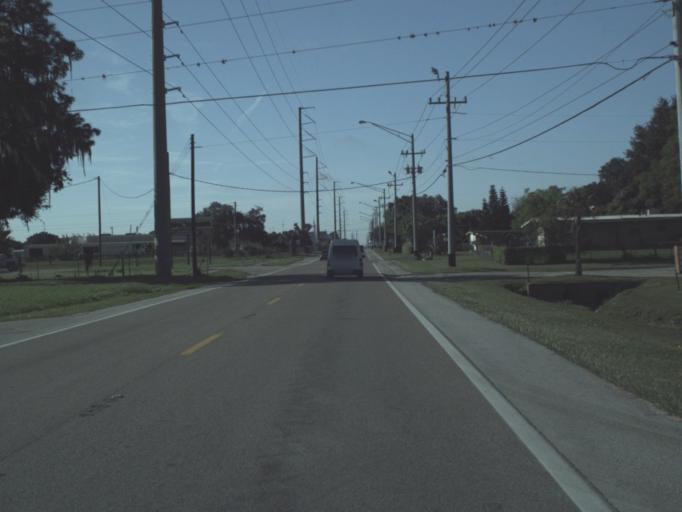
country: US
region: Florida
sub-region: Polk County
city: Crystal Lake
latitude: 28.0375
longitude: -81.9079
